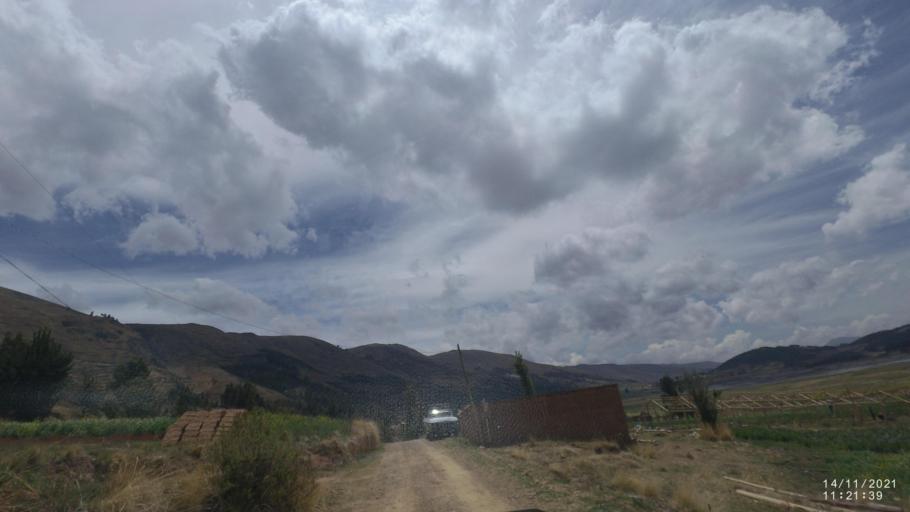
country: BO
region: Cochabamba
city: Cochabamba
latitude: -17.3363
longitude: -66.0353
